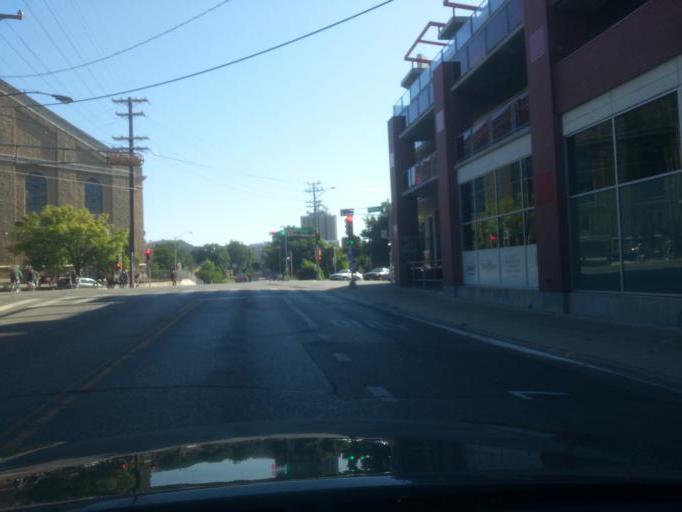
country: US
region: Wisconsin
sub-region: Dane County
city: Madison
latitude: 43.0676
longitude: -89.4132
